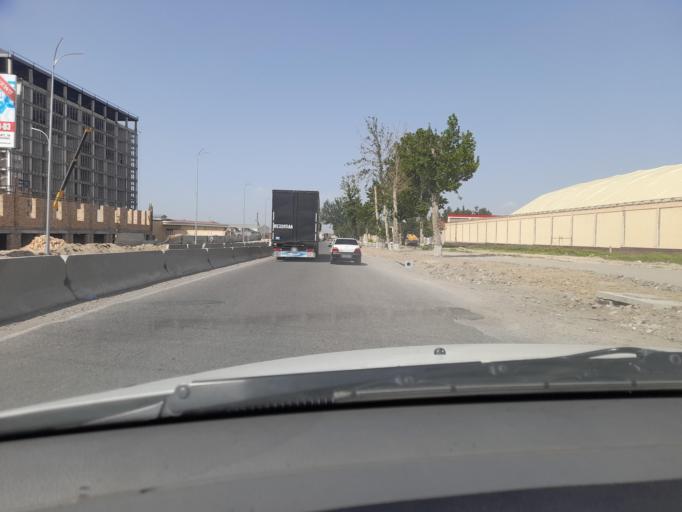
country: UZ
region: Samarqand
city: Samarqand
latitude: 39.6863
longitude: 67.0075
